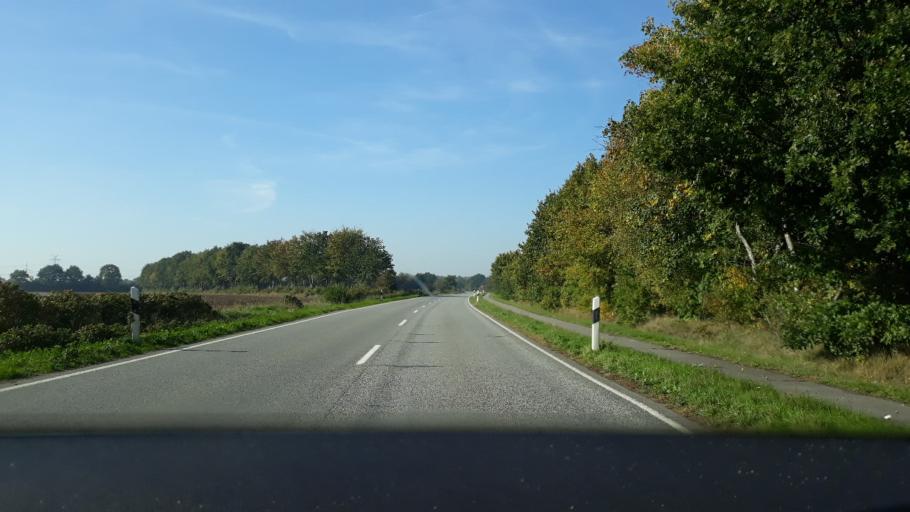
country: DE
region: Schleswig-Holstein
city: Kropp
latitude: 54.4029
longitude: 9.4851
